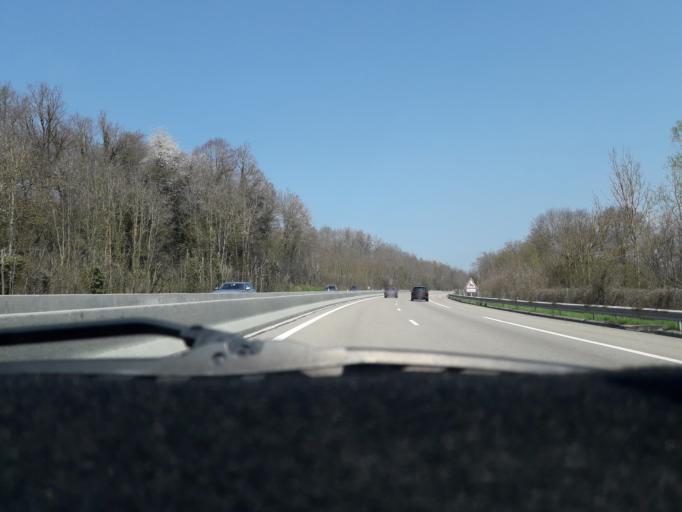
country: FR
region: Rhone-Alpes
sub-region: Departement de l'Isere
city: Chabons
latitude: 45.4485
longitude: 5.3995
